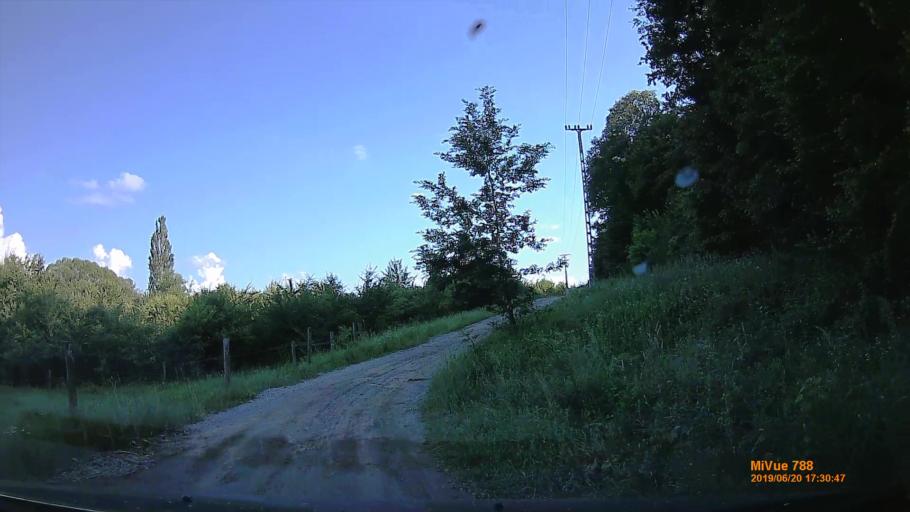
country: HU
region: Baranya
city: Buekkoesd
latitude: 46.1538
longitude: 18.0106
